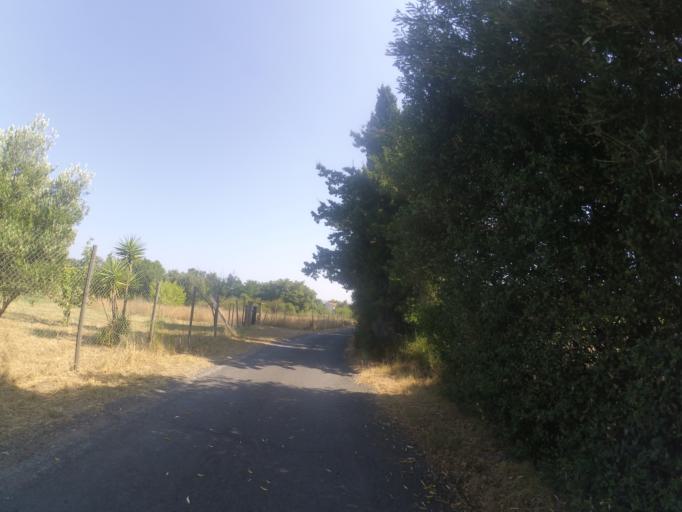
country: FR
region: Languedoc-Roussillon
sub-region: Departement des Pyrenees-Orientales
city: Ille-sur-Tet
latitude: 42.6609
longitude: 2.6256
